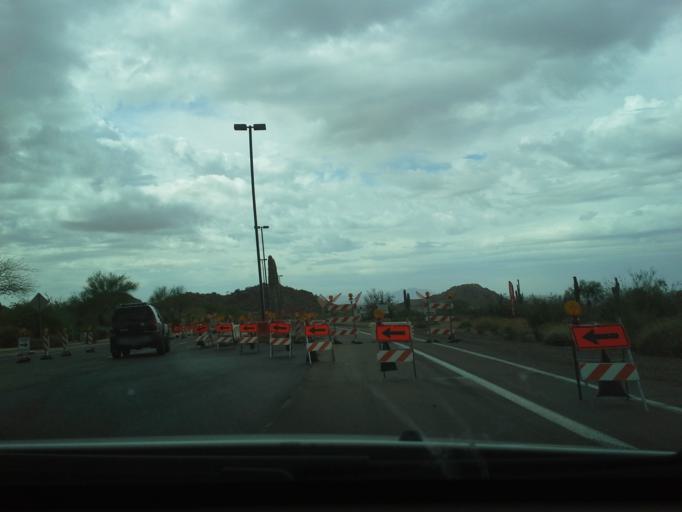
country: US
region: Arizona
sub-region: Pinal County
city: Apache Junction
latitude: 33.4600
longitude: -111.6324
